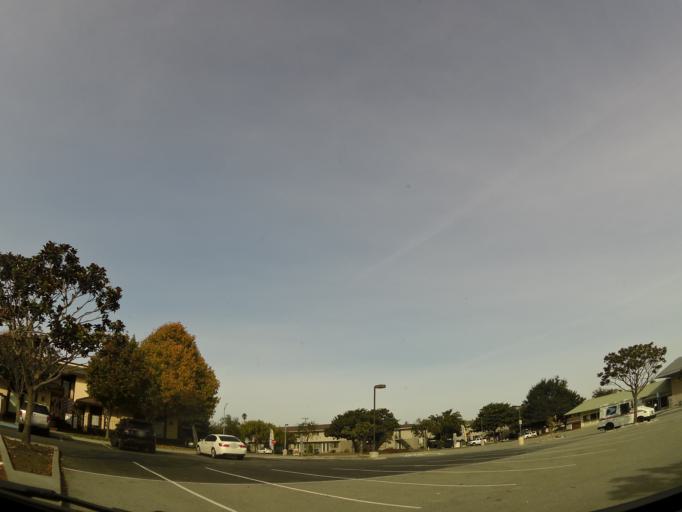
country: US
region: California
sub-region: Monterey County
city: Salinas
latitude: 36.6671
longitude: -121.6743
